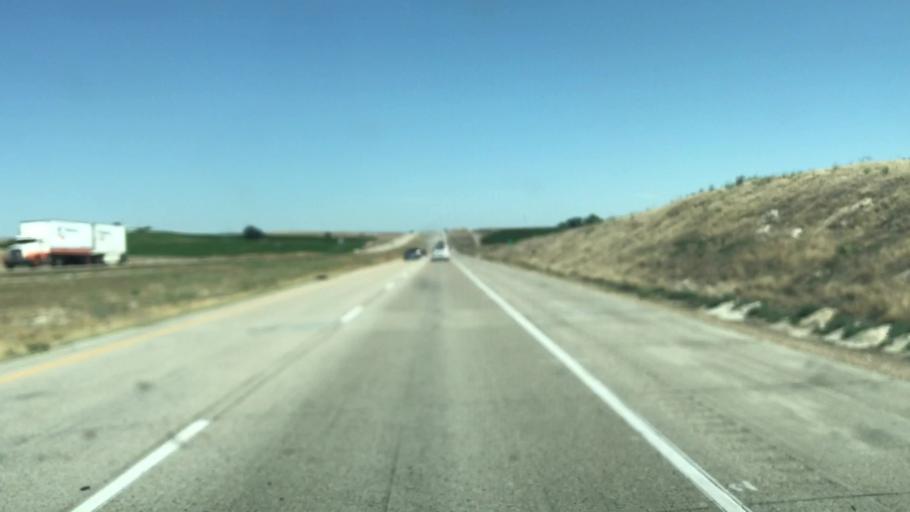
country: US
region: Idaho
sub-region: Payette County
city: New Plymouth
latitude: 43.8379
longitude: -116.7632
